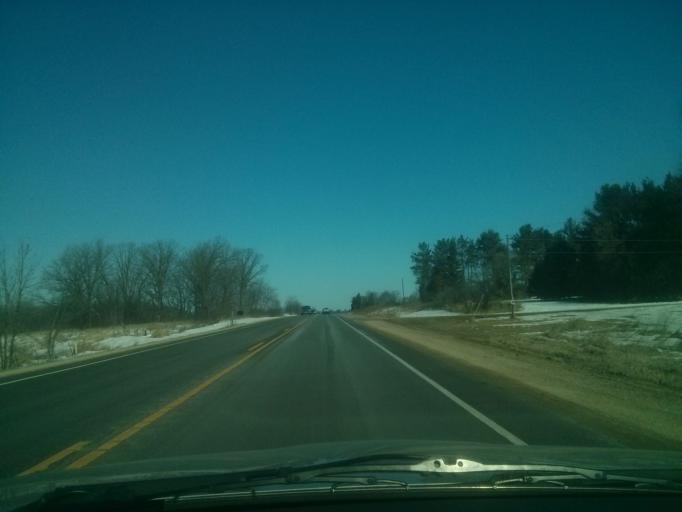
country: US
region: Wisconsin
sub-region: Polk County
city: Clear Lake
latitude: 45.1570
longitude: -92.2823
